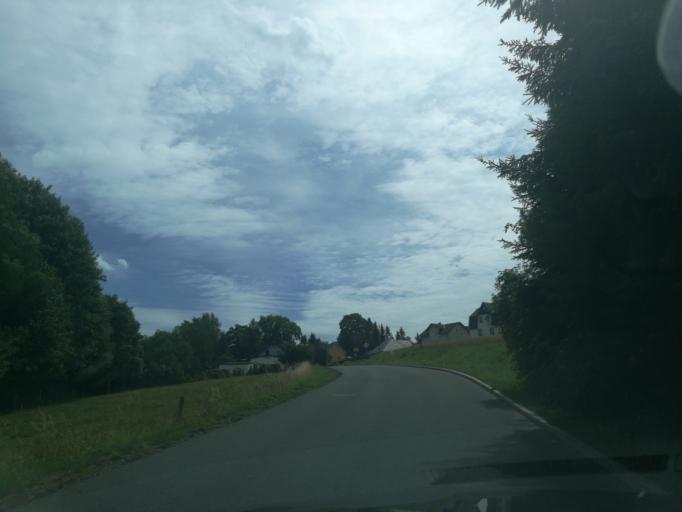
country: DE
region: Saxony
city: Adorf
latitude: 50.3124
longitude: 12.2676
